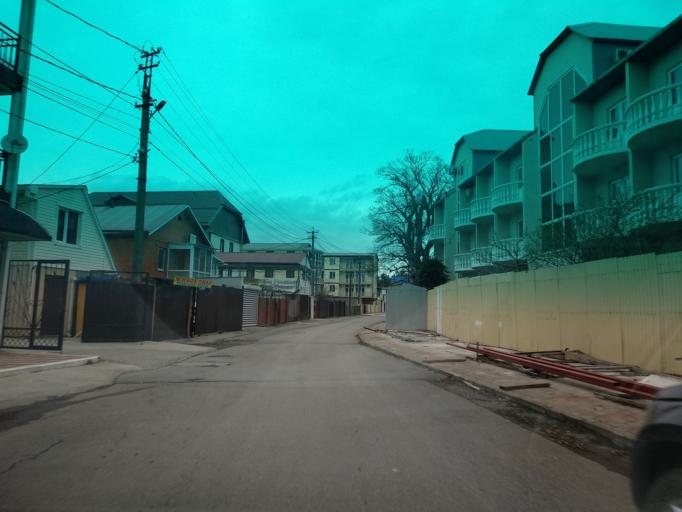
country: RU
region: Krasnodarskiy
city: Novomikhaylovskiy
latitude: 44.2390
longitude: 38.8373
